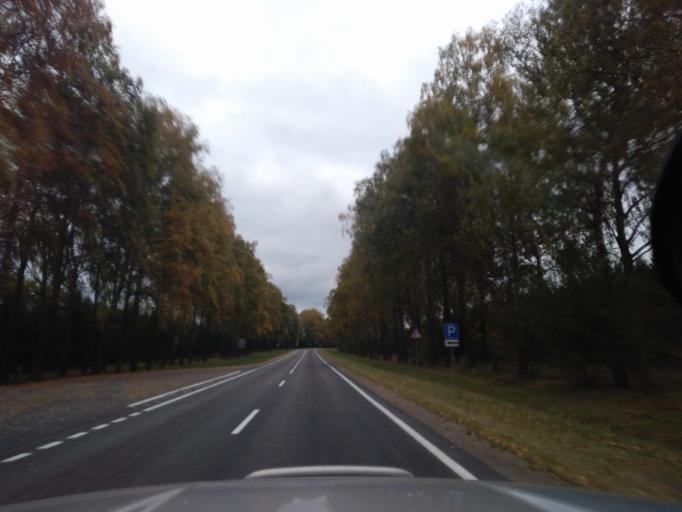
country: BY
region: Minsk
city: Slutsk
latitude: 53.2217
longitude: 27.4925
